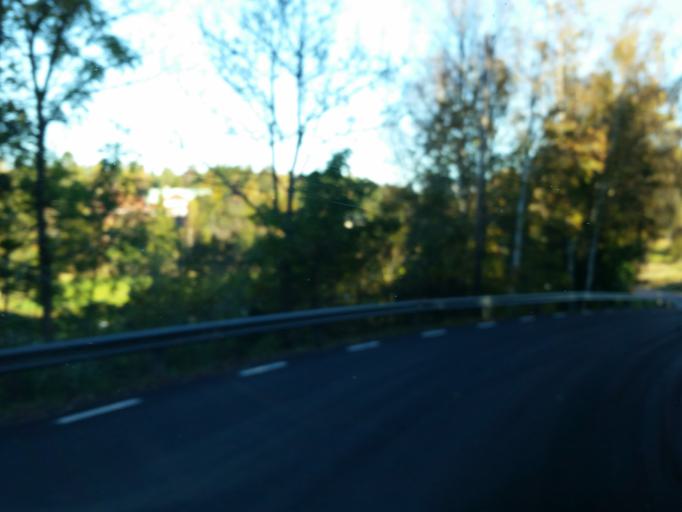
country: AX
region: Alands landsbygd
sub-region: Sund
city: Sund
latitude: 60.2241
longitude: 20.0914
